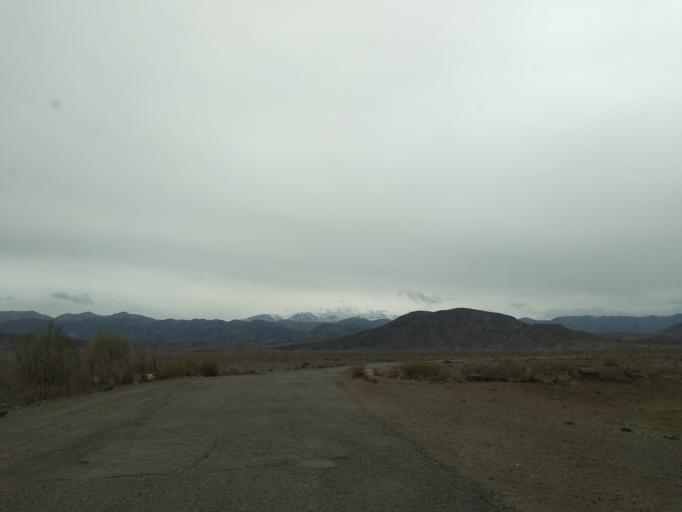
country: KG
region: Ysyk-Koel
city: Balykchy
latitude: 42.3200
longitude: 76.2342
